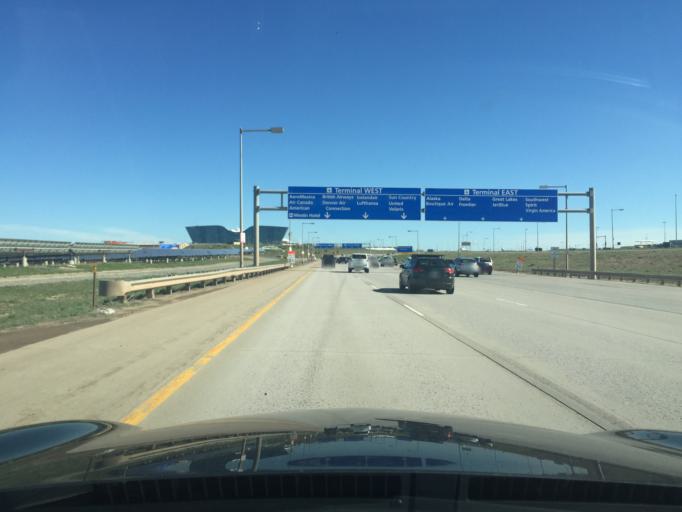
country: US
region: Colorado
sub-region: Weld County
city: Lochbuie
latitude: 39.8375
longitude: -104.6720
